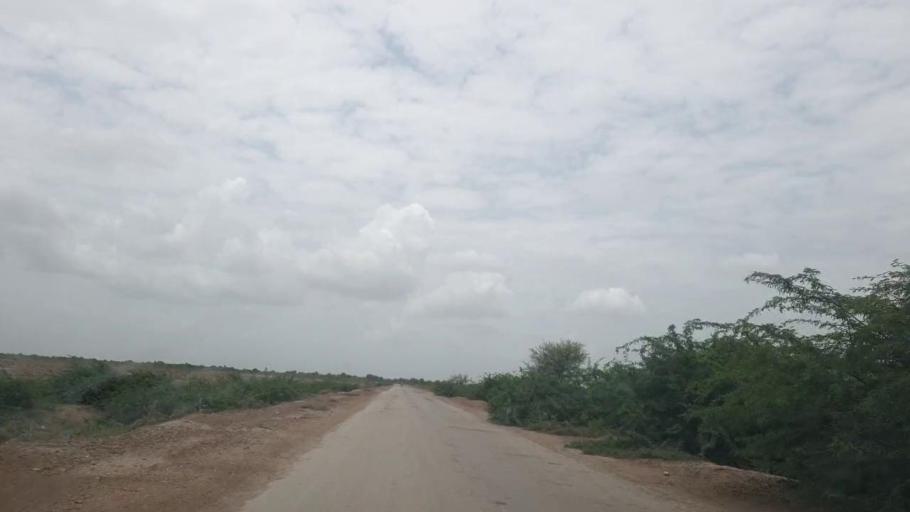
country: PK
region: Sindh
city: Naukot
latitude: 24.9492
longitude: 69.2817
